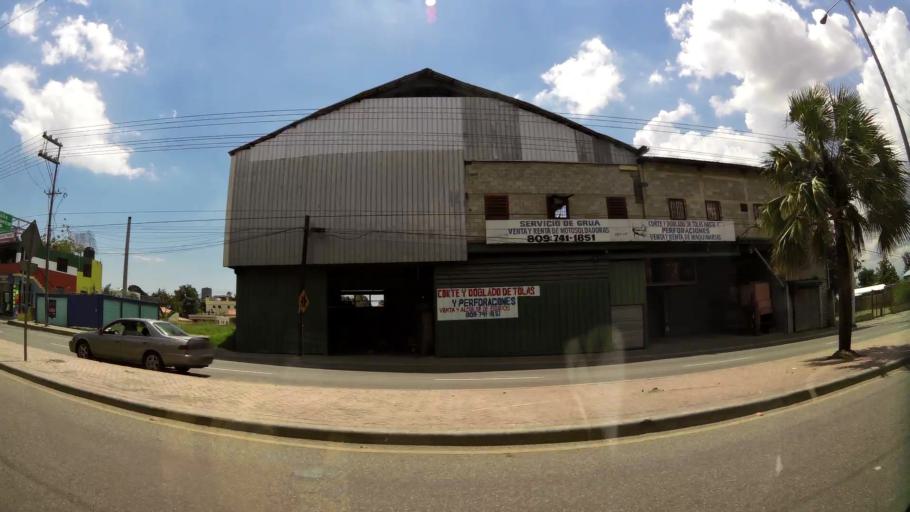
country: DO
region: Nacional
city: Ensanche Luperon
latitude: 18.5464
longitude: -69.9034
